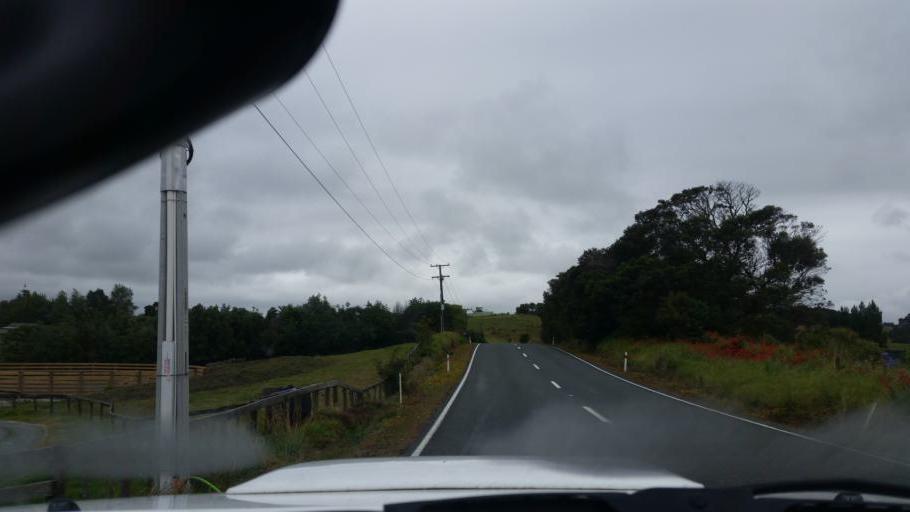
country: NZ
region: Auckland
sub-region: Auckland
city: Wellsford
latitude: -36.1589
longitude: 174.4556
